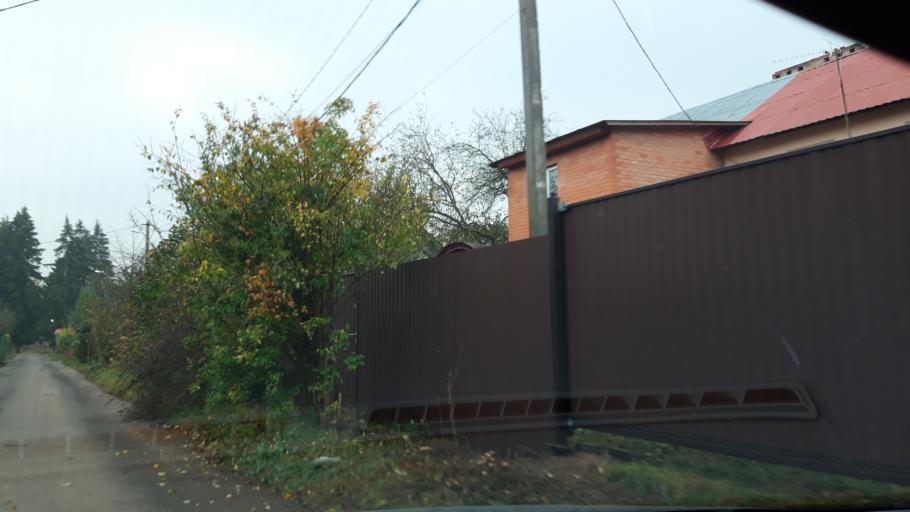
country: RU
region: Moskovskaya
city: Chashnikovo
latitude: 56.0213
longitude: 37.1832
